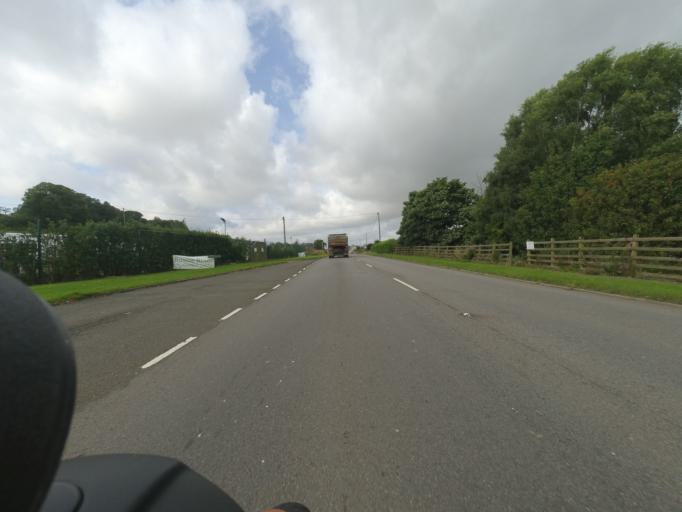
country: GB
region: Scotland
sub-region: Angus
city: Montrose
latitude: 56.6990
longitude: -2.4846
